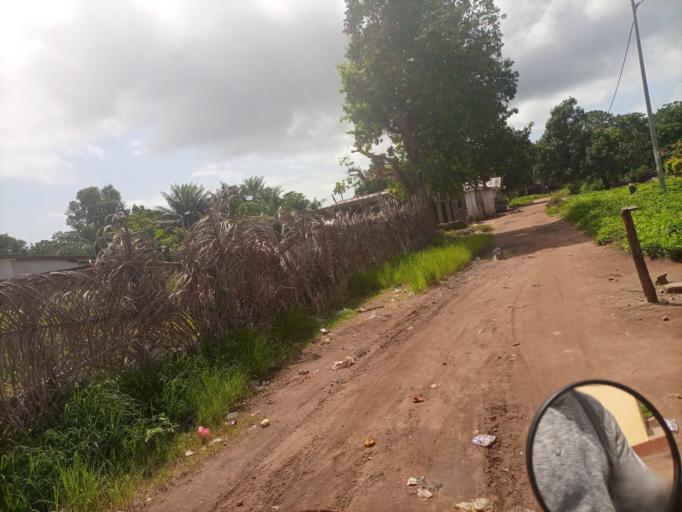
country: SL
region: Northern Province
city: Tintafor
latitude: 8.6369
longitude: -13.2141
